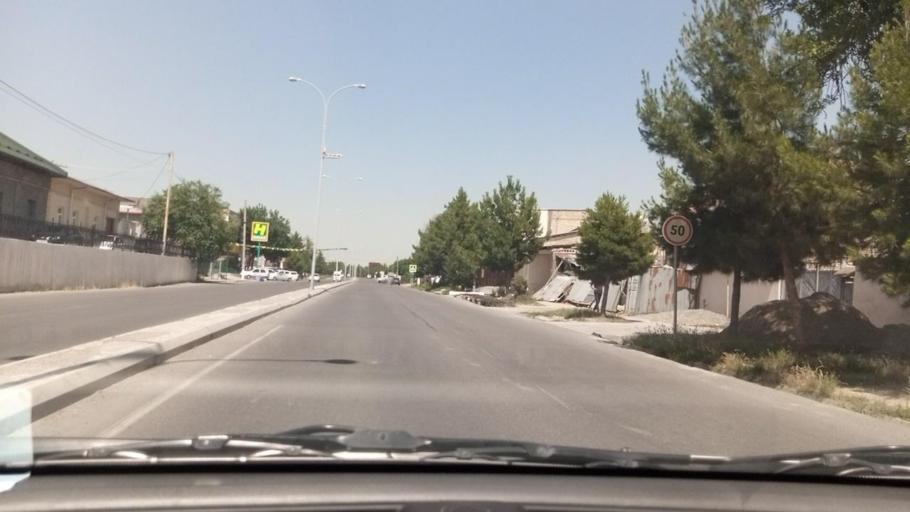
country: UZ
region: Toshkent Shahri
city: Tashkent
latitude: 41.2435
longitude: 69.2008
